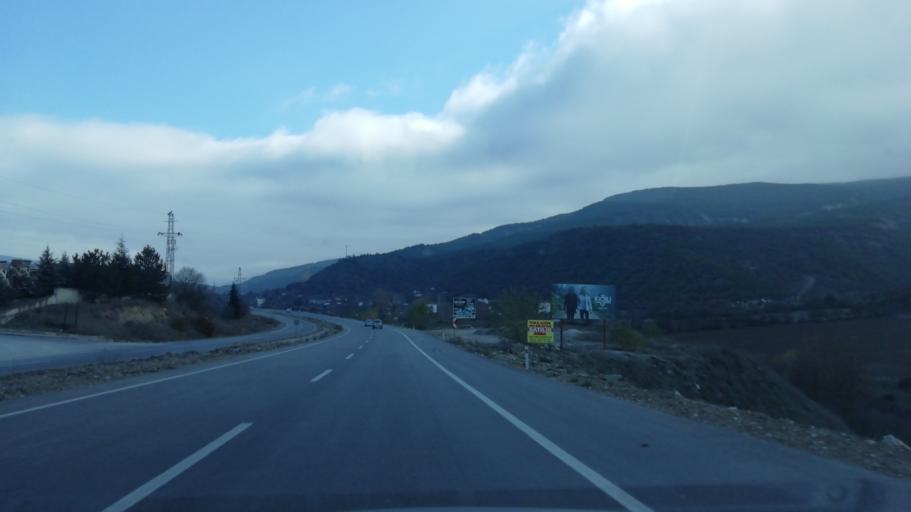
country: TR
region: Karabuk
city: Safranbolu
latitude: 41.2177
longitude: 32.7297
